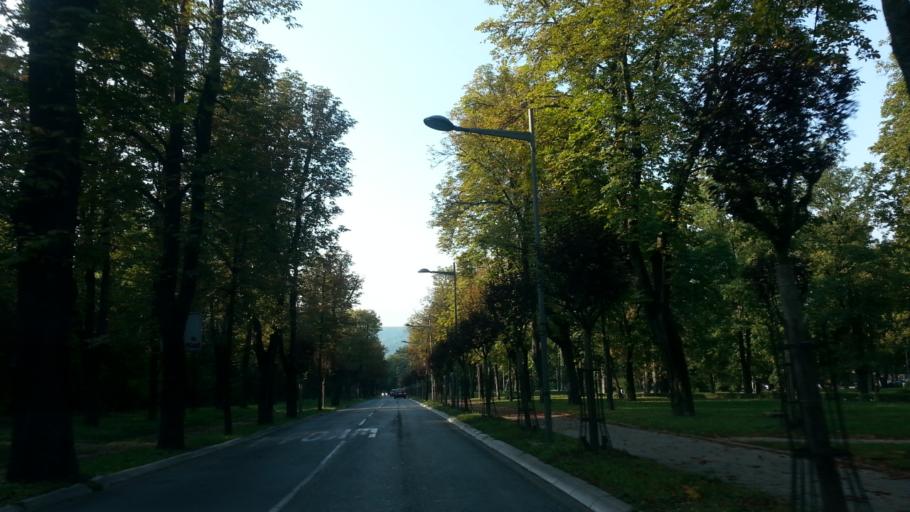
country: RS
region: Central Serbia
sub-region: Belgrade
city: Savski Venac
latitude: 44.7875
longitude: 20.4428
